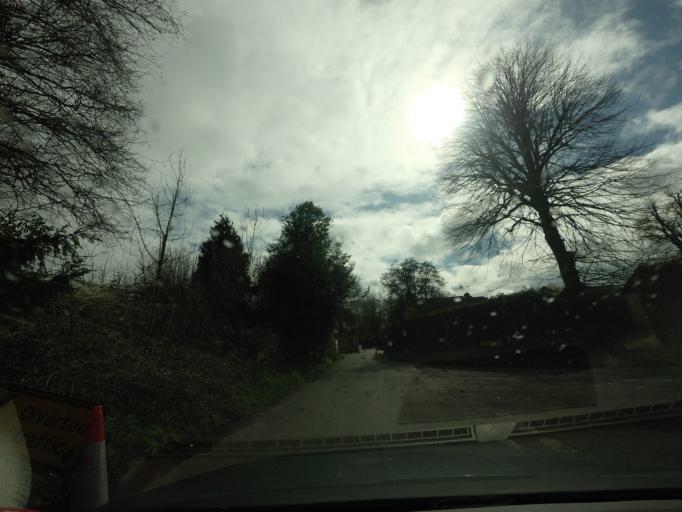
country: GB
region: England
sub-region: Kent
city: Borough Green
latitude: 51.2670
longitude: 0.2736
